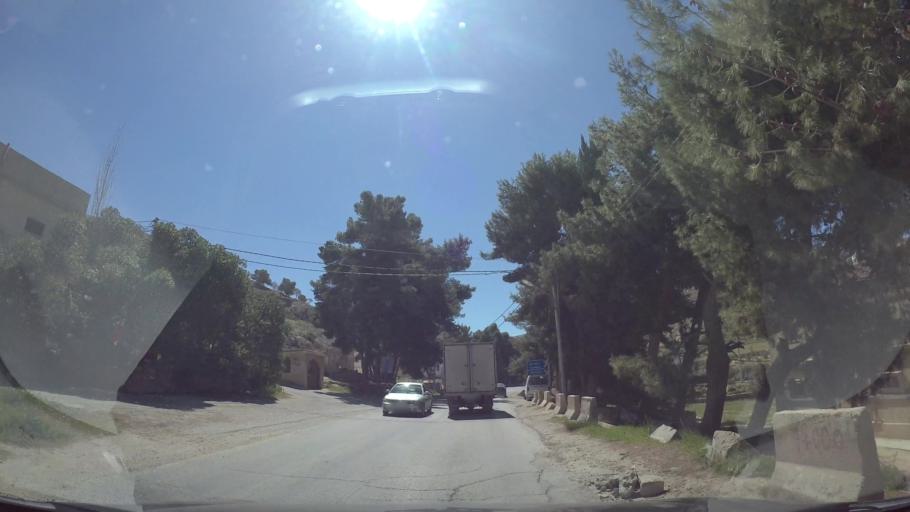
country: JO
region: Tafielah
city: At Tafilah
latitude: 30.8190
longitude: 35.5867
